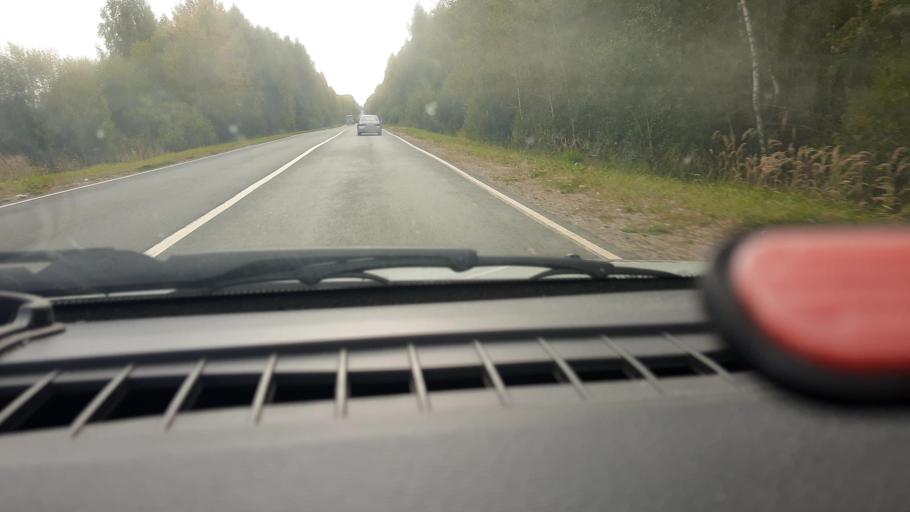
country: RU
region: Nizjnij Novgorod
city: Uren'
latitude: 57.2726
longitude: 45.6288
